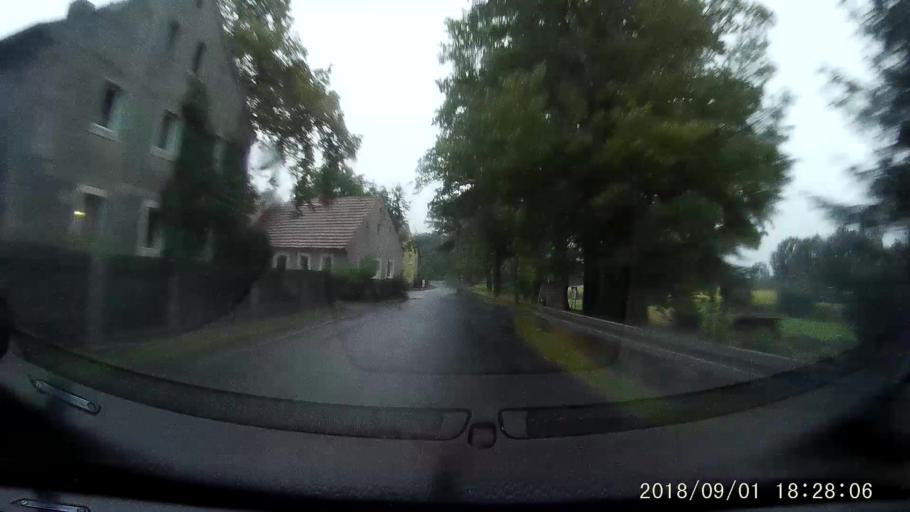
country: PL
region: Lower Silesian Voivodeship
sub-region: Powiat zgorzelecki
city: Piensk
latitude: 51.2114
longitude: 15.0434
